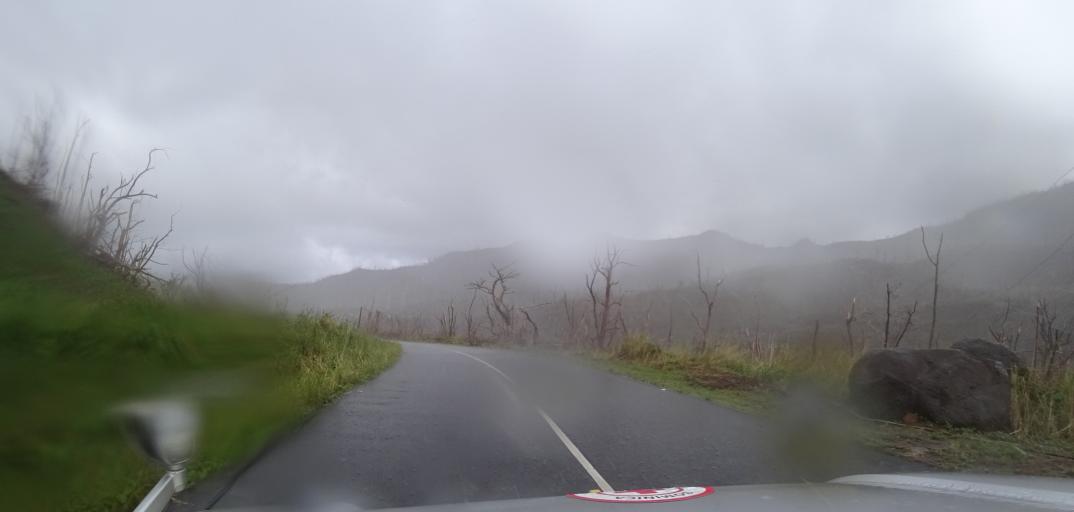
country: DM
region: Saint Andrew
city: Marigot
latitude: 15.4852
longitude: -61.2779
